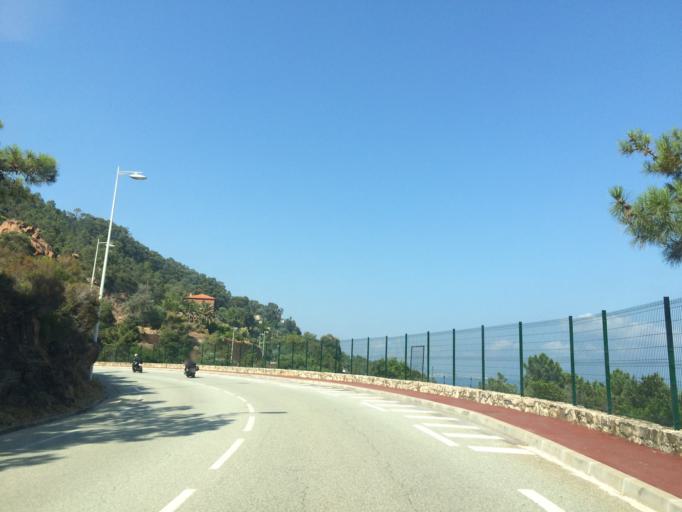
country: FR
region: Provence-Alpes-Cote d'Azur
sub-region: Departement des Alpes-Maritimes
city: Theoule-sur-Mer
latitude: 43.4946
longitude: 6.9448
